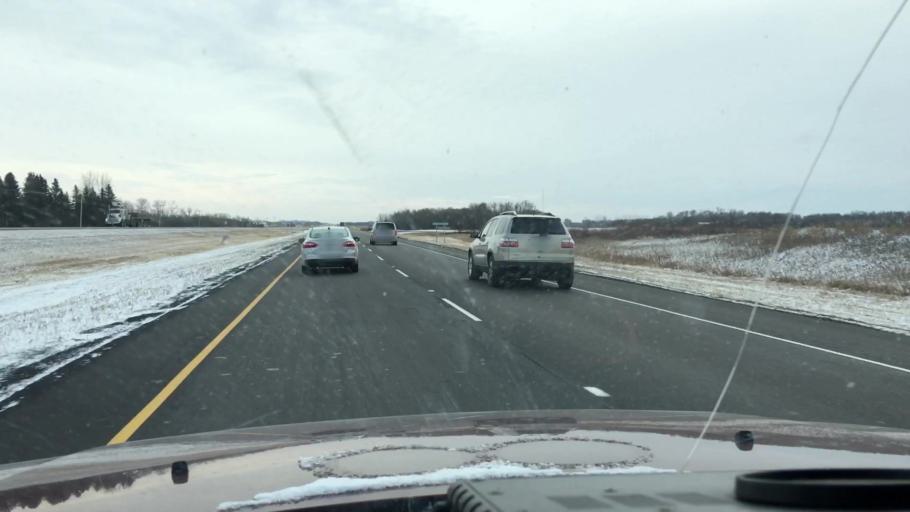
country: CA
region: Saskatchewan
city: Saskatoon
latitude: 52.0156
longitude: -106.5753
